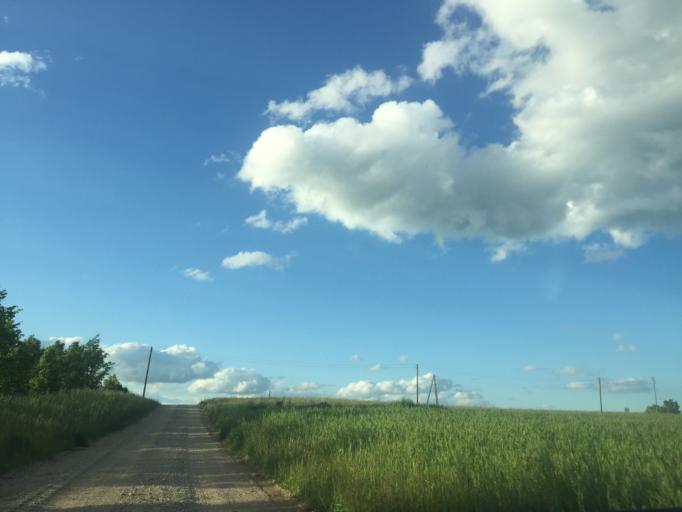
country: LV
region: Kandava
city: Kandava
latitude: 57.0047
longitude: 22.7368
